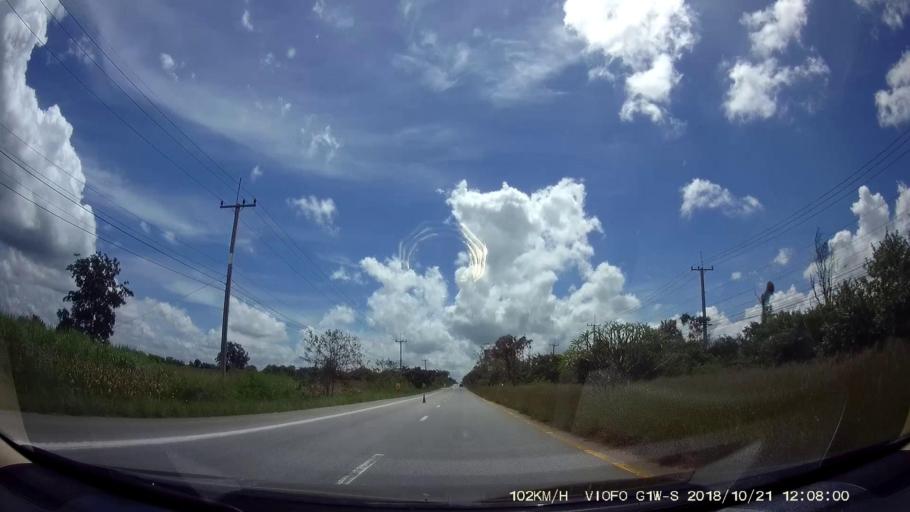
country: TH
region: Chaiyaphum
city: Chatturat
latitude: 15.4405
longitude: 101.8299
